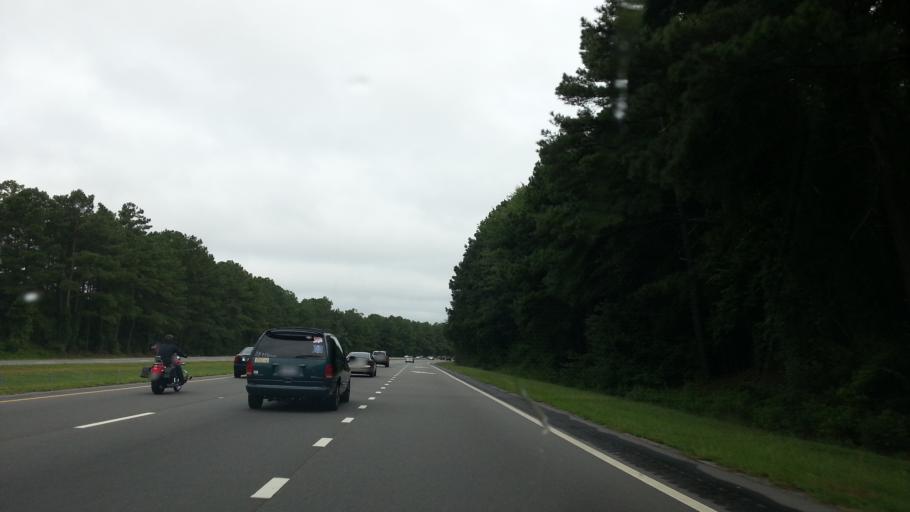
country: US
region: North Carolina
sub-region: Cumberland County
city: Fort Bragg
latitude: 35.0773
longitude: -78.9605
